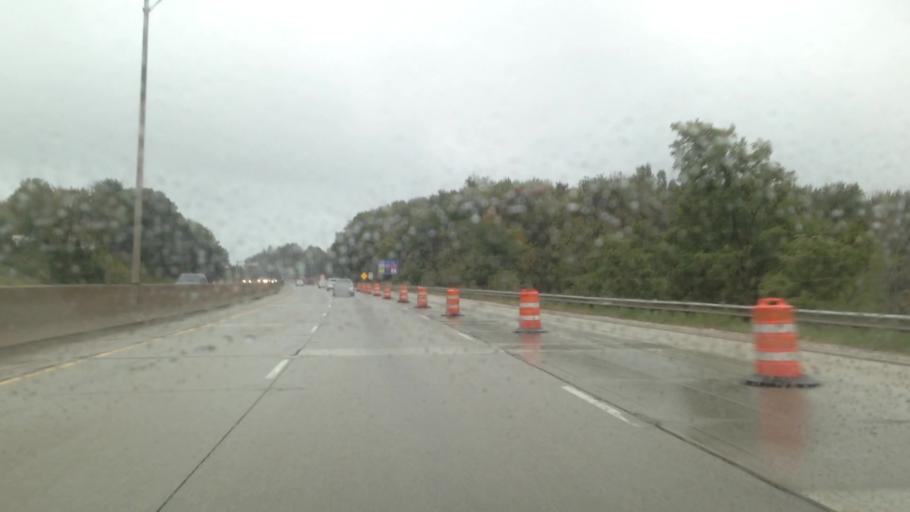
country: US
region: Ohio
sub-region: Summit County
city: Silver Lake
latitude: 41.1759
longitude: -81.4794
